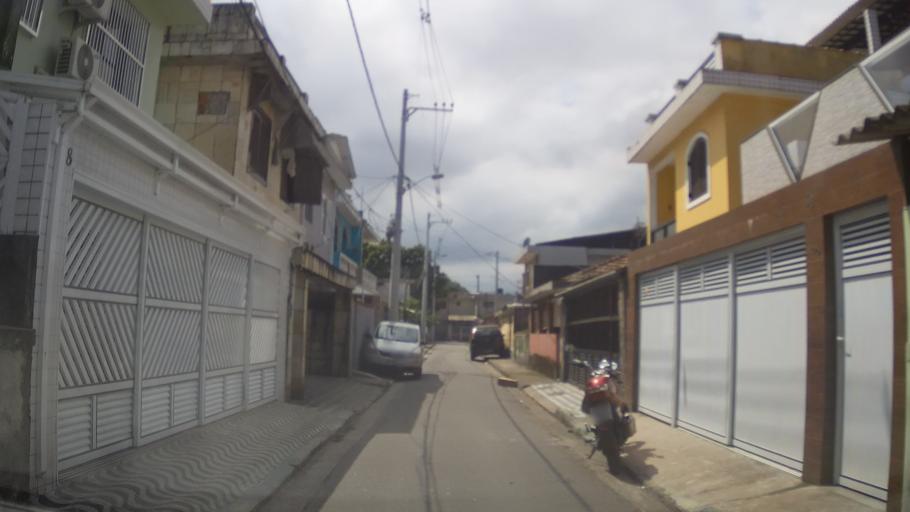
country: BR
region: Sao Paulo
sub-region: Santos
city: Santos
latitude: -23.9665
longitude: -46.3078
